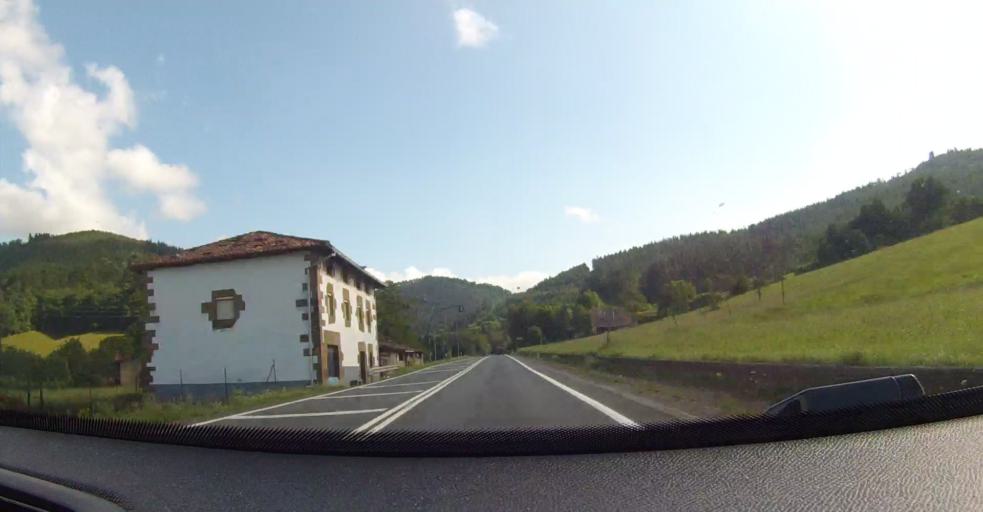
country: ES
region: Basque Country
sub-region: Bizkaia
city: Muxika
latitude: 43.2702
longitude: -2.6856
